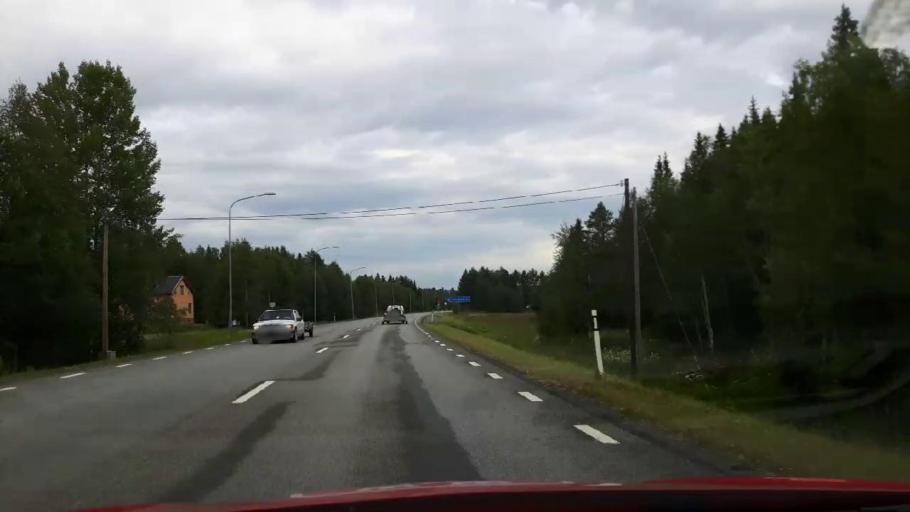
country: SE
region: Jaemtland
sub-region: Stroemsunds Kommun
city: Stroemsund
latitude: 63.6714
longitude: 15.3922
